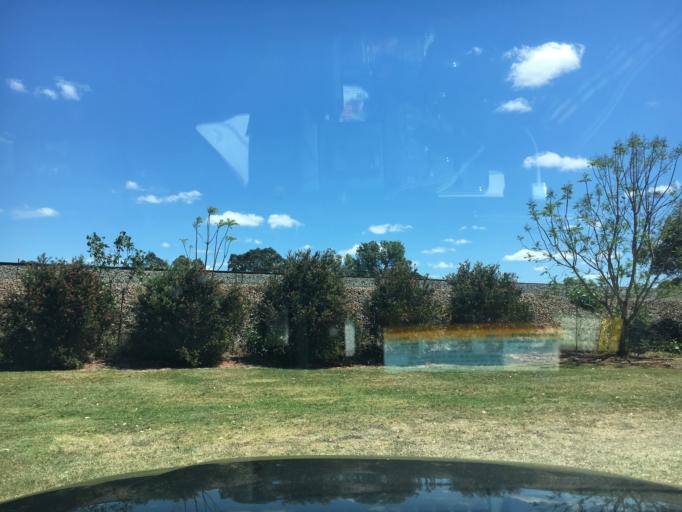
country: AU
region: New South Wales
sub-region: Singleton
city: Singleton
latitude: -32.5664
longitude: 151.1599
